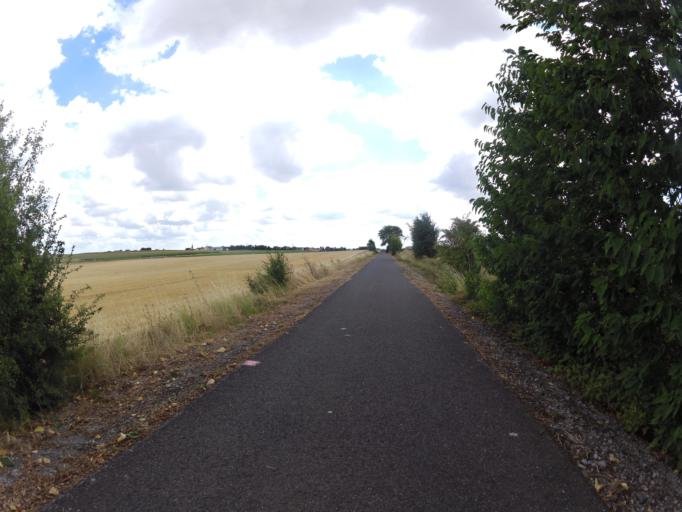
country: DE
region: Bavaria
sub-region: Regierungsbezirk Unterfranken
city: Sonderhofen
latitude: 49.5804
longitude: 10.0100
